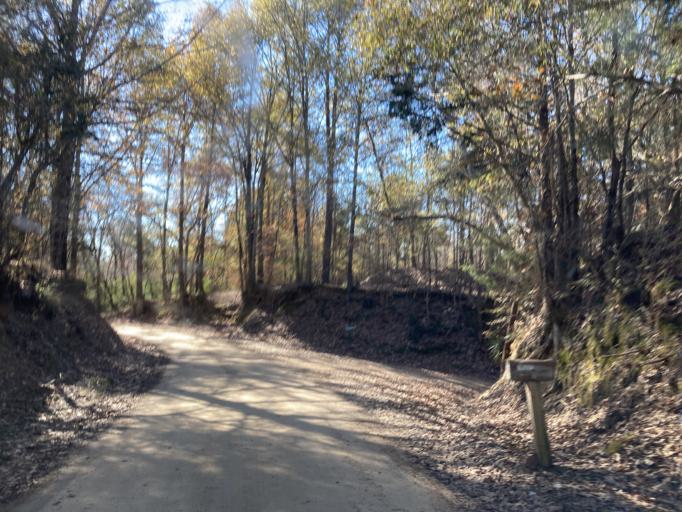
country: US
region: Mississippi
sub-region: Madison County
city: Kearney Park
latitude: 32.6189
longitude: -90.4567
